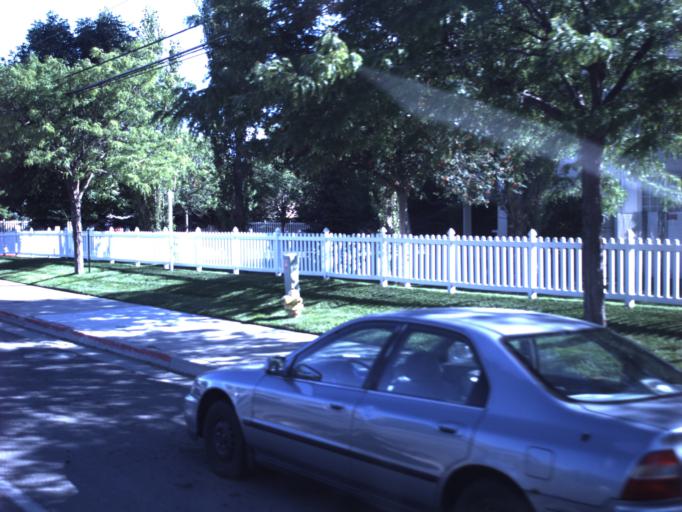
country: US
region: Utah
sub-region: Utah County
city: Lindon
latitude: 40.3308
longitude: -111.7113
